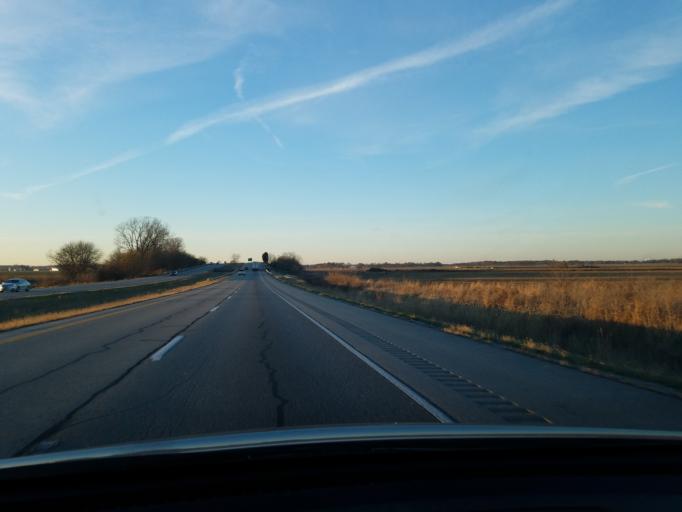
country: US
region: Indiana
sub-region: Posey County
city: Poseyville
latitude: 38.1780
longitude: -87.7603
